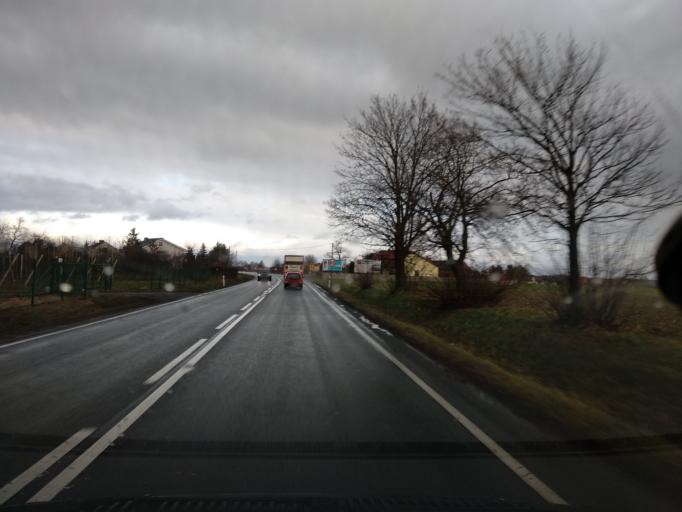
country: PL
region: Greater Poland Voivodeship
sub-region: Powiat koninski
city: Stare Miasto
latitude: 52.1515
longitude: 18.2035
